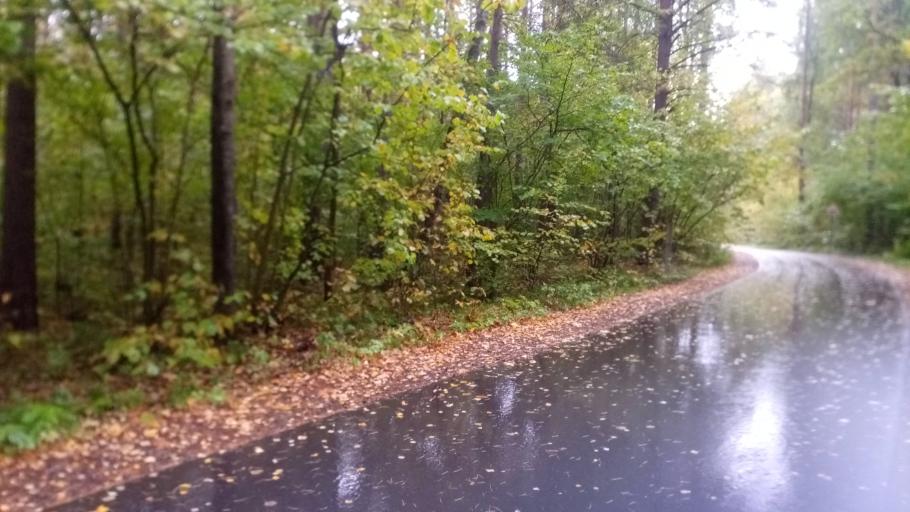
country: RU
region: Tatarstan
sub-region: Tukayevskiy Rayon
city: Naberezhnyye Chelny
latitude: 55.8464
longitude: 52.4670
